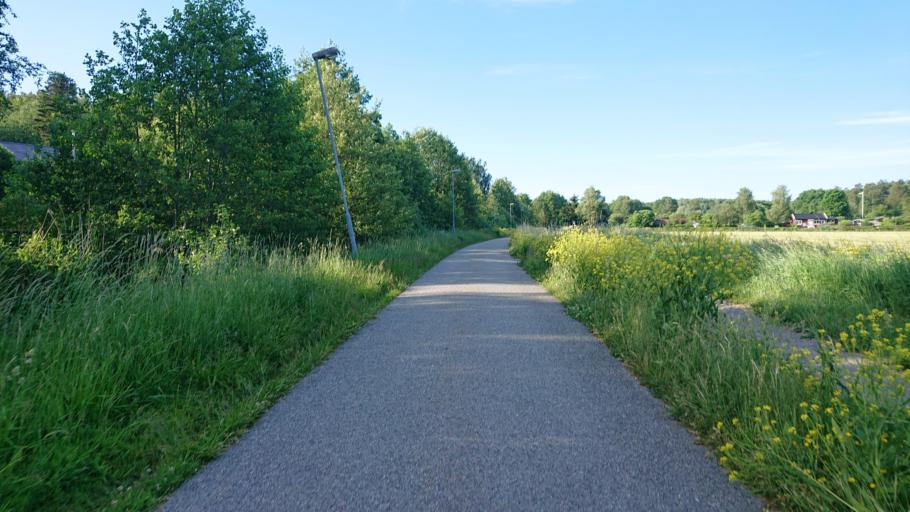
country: SE
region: Stockholm
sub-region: Osterakers Kommun
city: Akersberga
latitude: 59.4951
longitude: 18.2907
